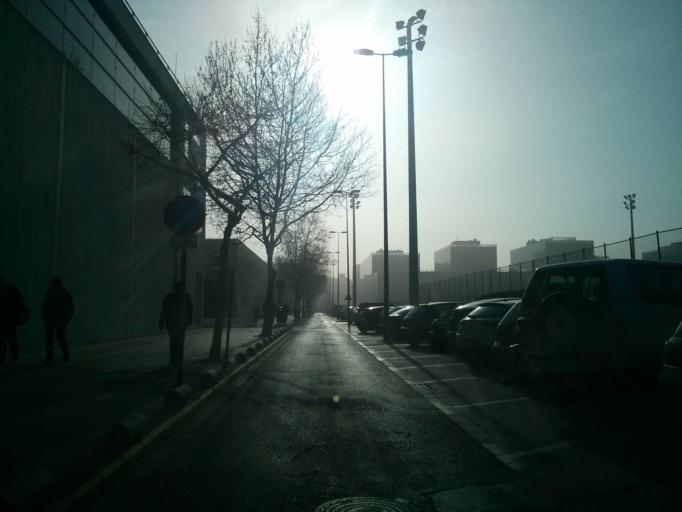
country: ES
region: Valencia
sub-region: Provincia de Valencia
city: Alboraya
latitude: 39.4797
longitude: -0.3362
